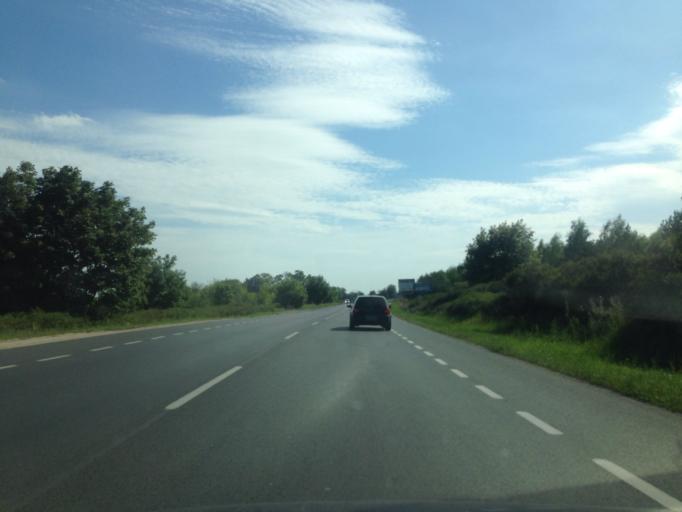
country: PL
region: Kujawsko-Pomorskie
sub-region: Torun
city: Torun
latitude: 53.0446
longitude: 18.6159
